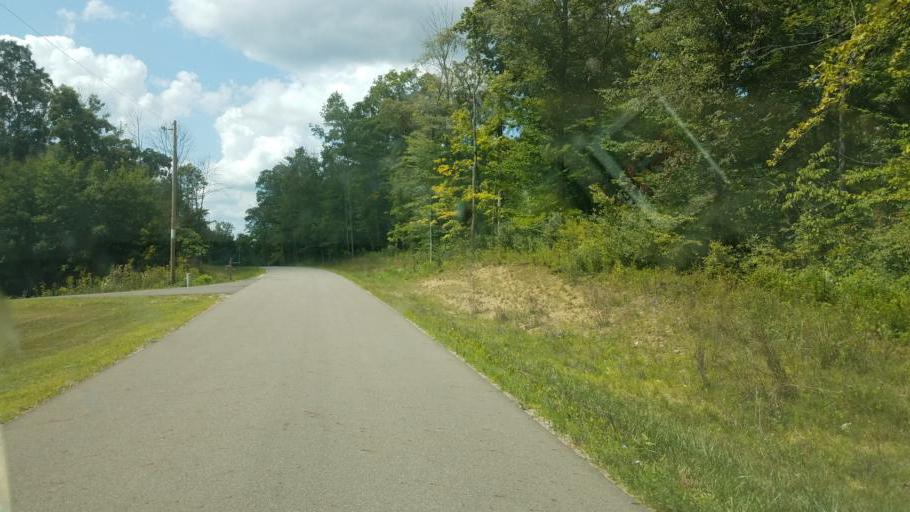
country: US
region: Ohio
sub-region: Morrow County
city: Cardington
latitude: 40.4325
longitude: -82.7959
